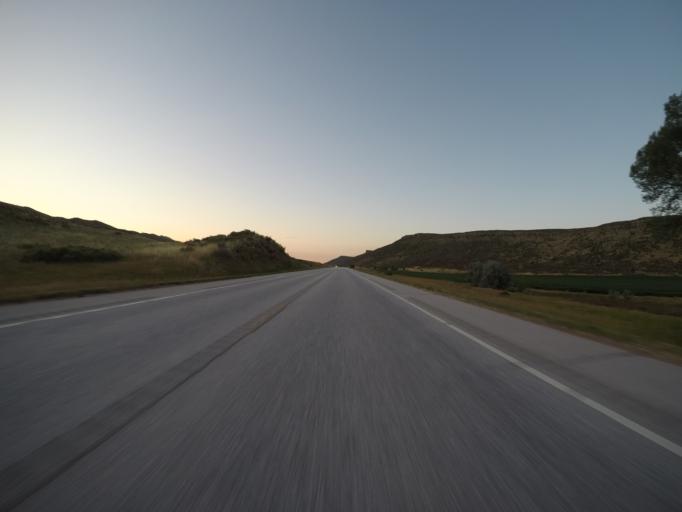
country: US
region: Colorado
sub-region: Larimer County
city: Laporte
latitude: 40.6856
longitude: -105.1767
